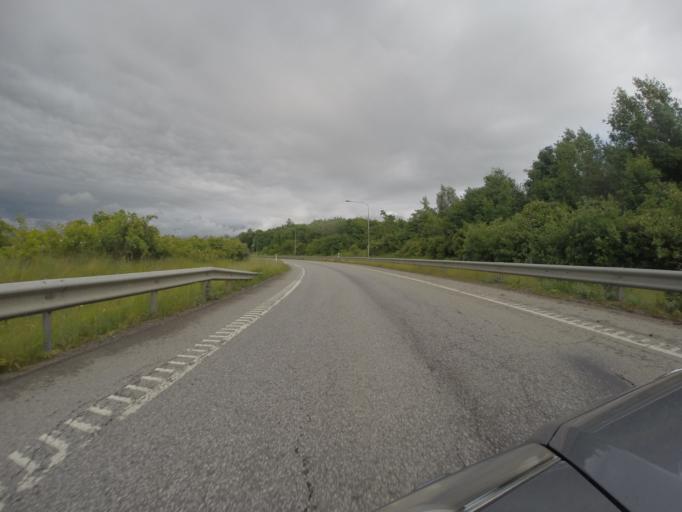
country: SE
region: Skane
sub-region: Burlovs Kommun
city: Arloev
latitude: 55.6027
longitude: 13.0696
